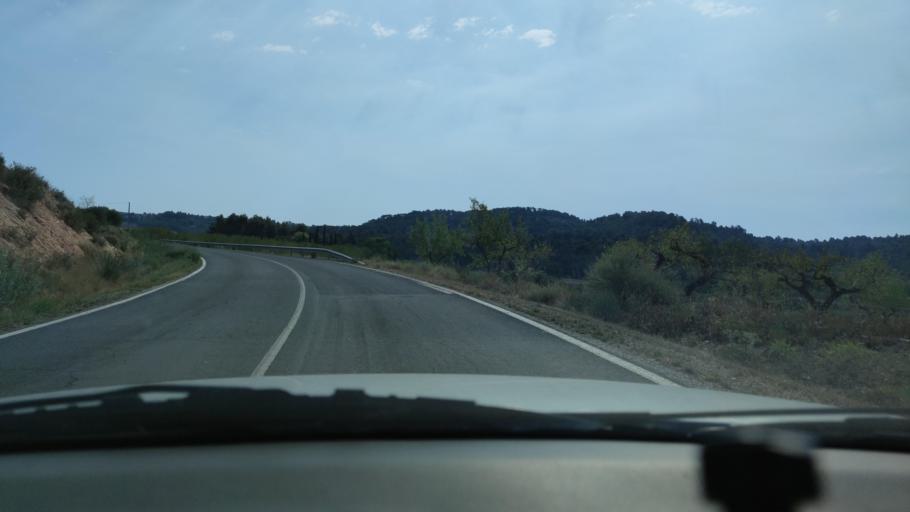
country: ES
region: Catalonia
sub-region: Provincia de Lleida
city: Arbeca
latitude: 41.5015
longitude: 0.9681
